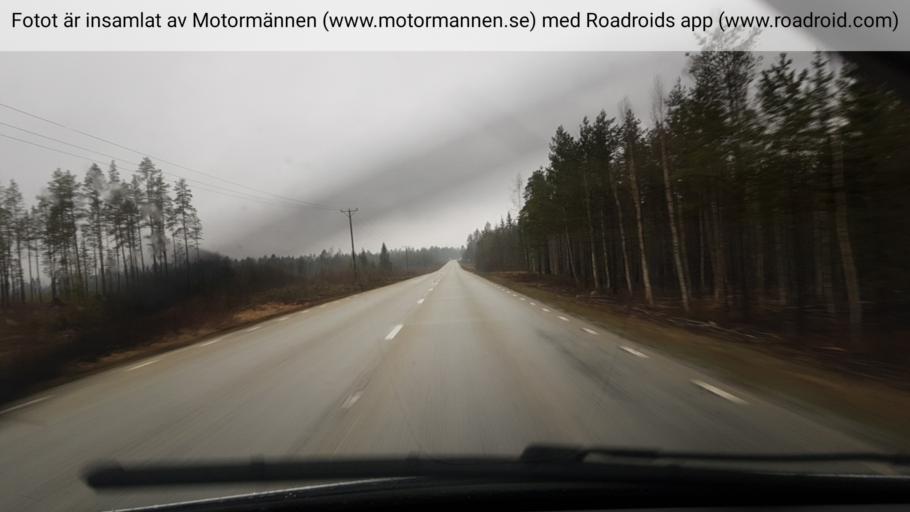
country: SE
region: Jaemtland
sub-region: Bergs Kommun
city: Hoverberg
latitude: 62.4965
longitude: 14.2115
